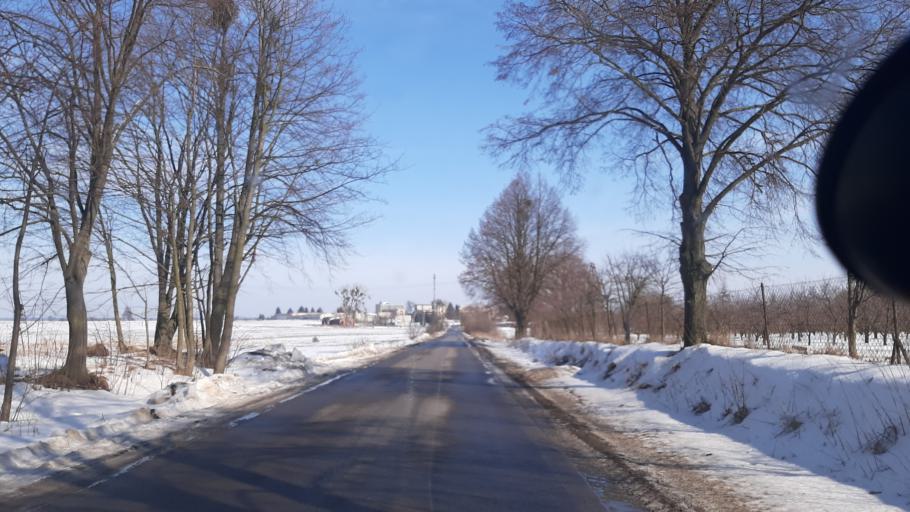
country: PL
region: Lublin Voivodeship
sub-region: Powiat pulawski
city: Kurow
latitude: 51.3818
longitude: 22.1624
